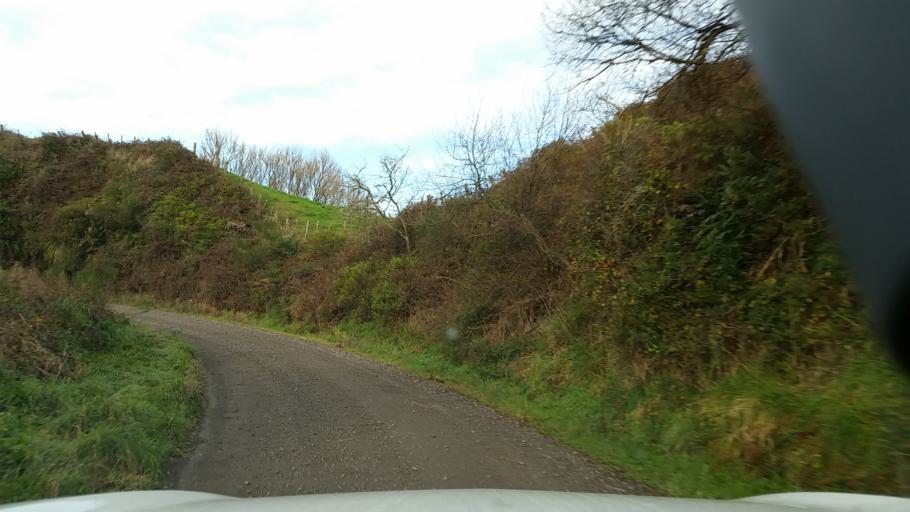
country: NZ
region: Bay of Plenty
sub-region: Rotorua District
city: Rotorua
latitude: -38.2684
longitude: 176.1548
